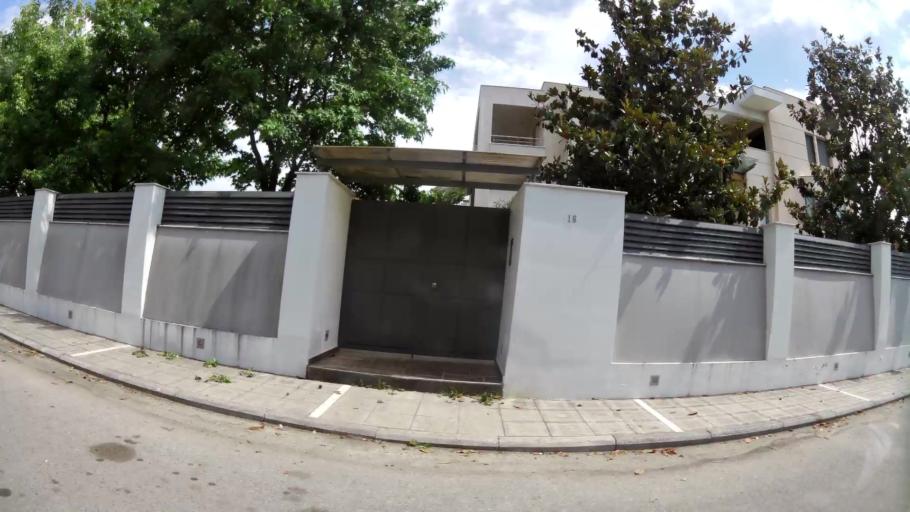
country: GR
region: Central Macedonia
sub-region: Nomos Pierias
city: Katerini
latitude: 40.2782
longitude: 22.4989
